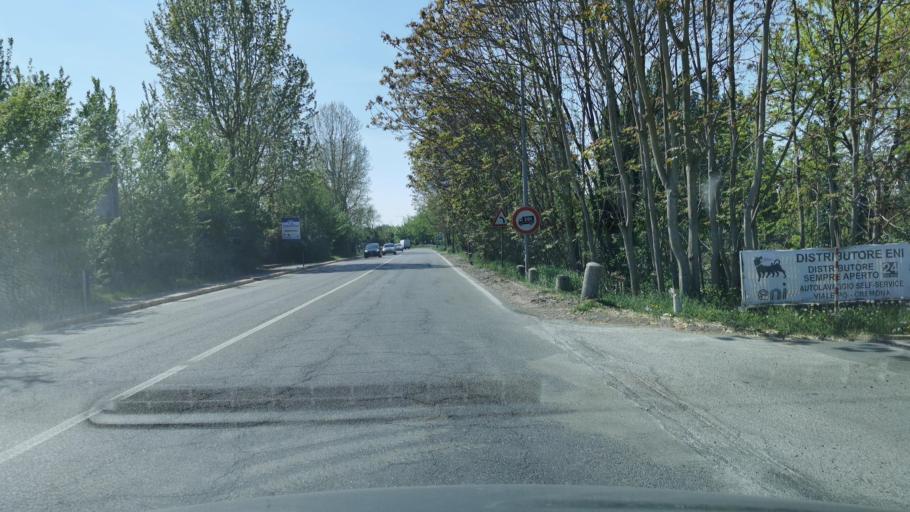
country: IT
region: Lombardy
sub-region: Provincia di Cremona
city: Cremona
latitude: 45.1303
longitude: 9.9988
